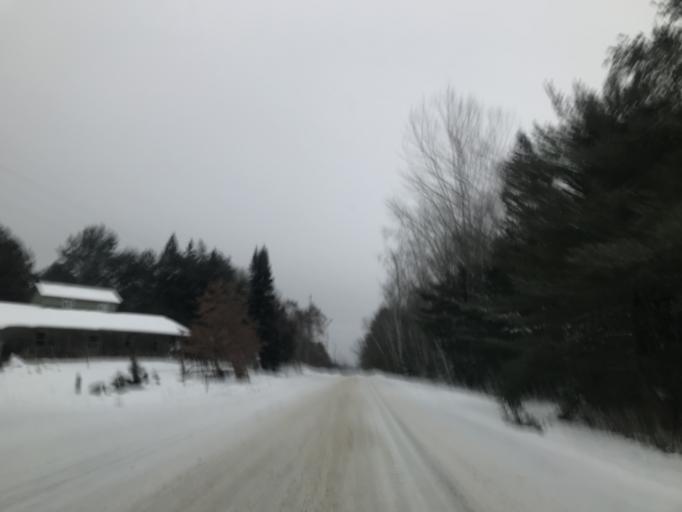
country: US
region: Wisconsin
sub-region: Marinette County
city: Peshtigo
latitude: 45.0640
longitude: -87.7378
